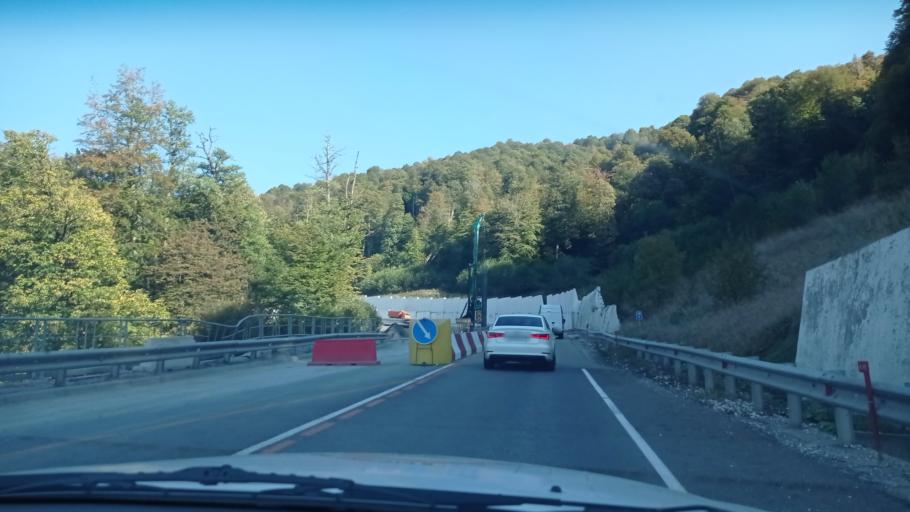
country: RU
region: Krasnodarskiy
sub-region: Sochi City
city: Krasnaya Polyana
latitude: 43.6597
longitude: 40.3064
